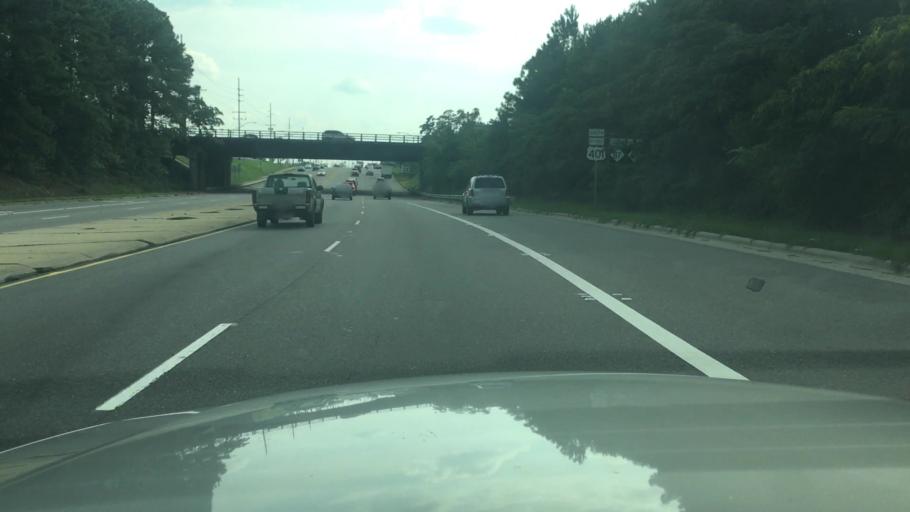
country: US
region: North Carolina
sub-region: Cumberland County
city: Fort Bragg
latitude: 35.0870
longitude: -78.9493
